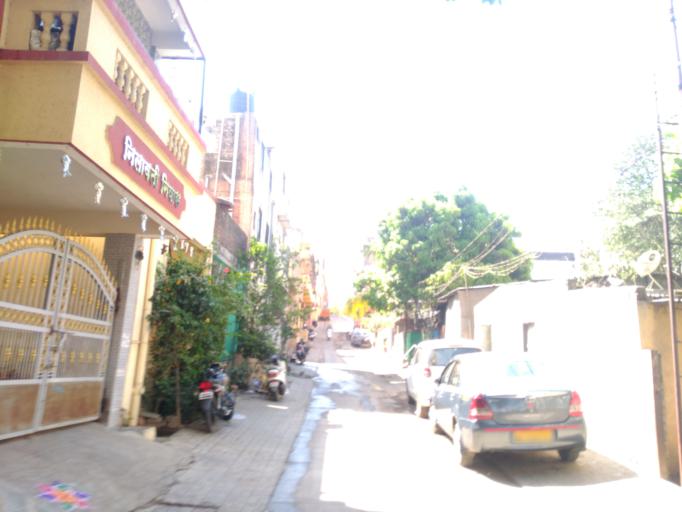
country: IN
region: Maharashtra
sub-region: Pune Division
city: Pune
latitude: 18.4474
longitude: 73.8767
